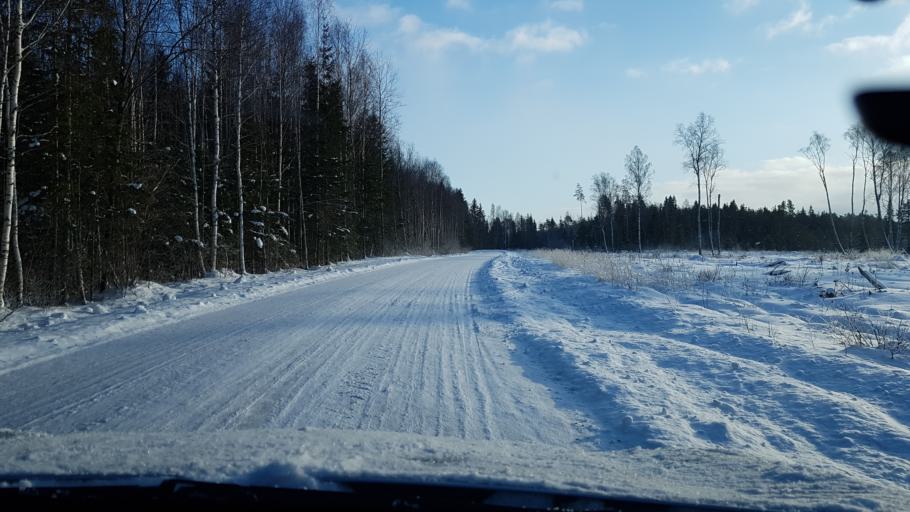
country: EE
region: Harju
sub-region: Nissi vald
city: Turba
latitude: 59.1336
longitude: 24.1942
